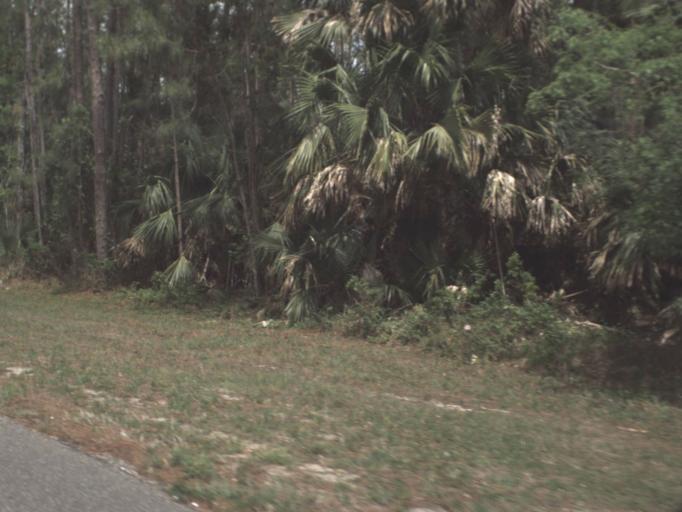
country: US
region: Florida
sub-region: Flagler County
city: Bunnell
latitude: 29.3992
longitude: -81.3071
